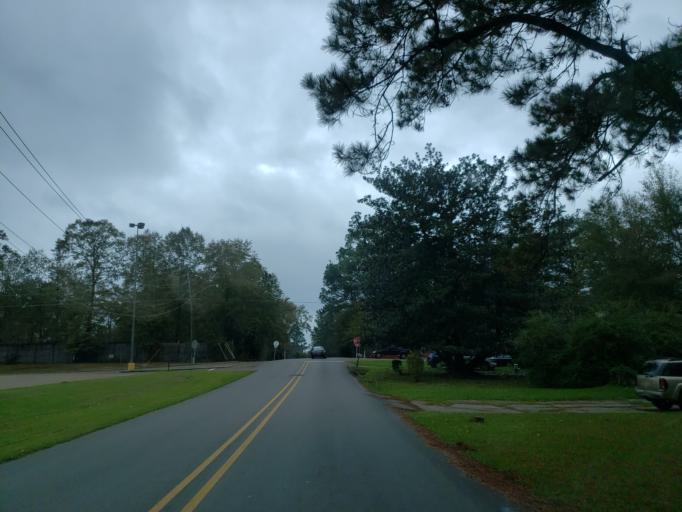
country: US
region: Mississippi
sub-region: Forrest County
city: Hattiesburg
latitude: 31.3133
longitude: -89.3154
